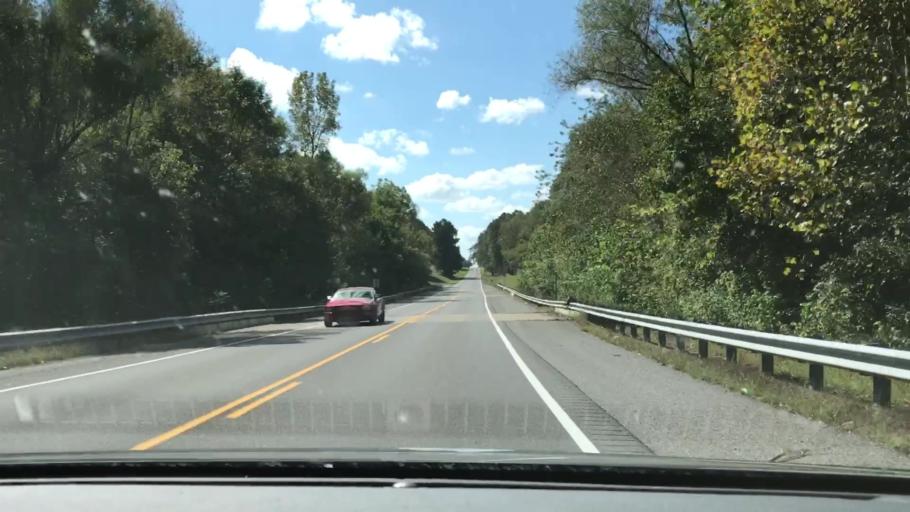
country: US
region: Kentucky
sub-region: McCracken County
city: Reidland
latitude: 36.9111
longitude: -88.5219
